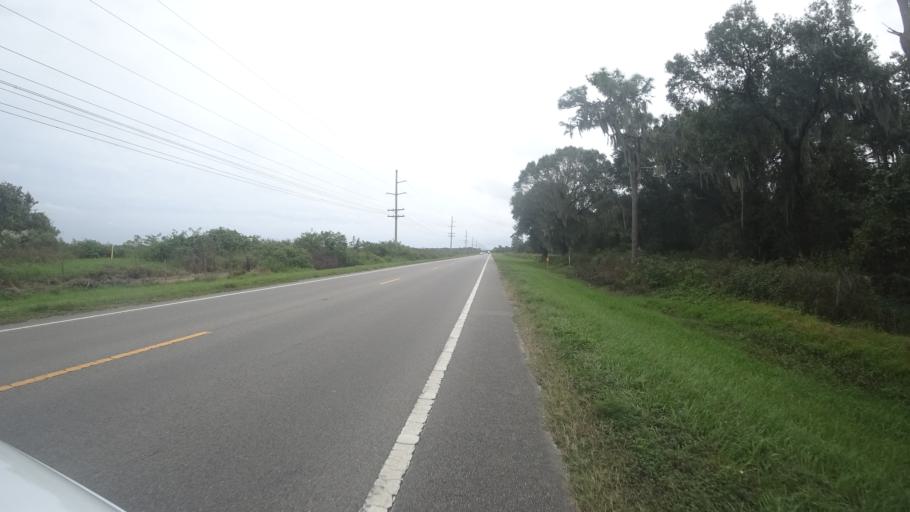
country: US
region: Florida
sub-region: Hillsborough County
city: Wimauma
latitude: 27.5893
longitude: -82.1412
